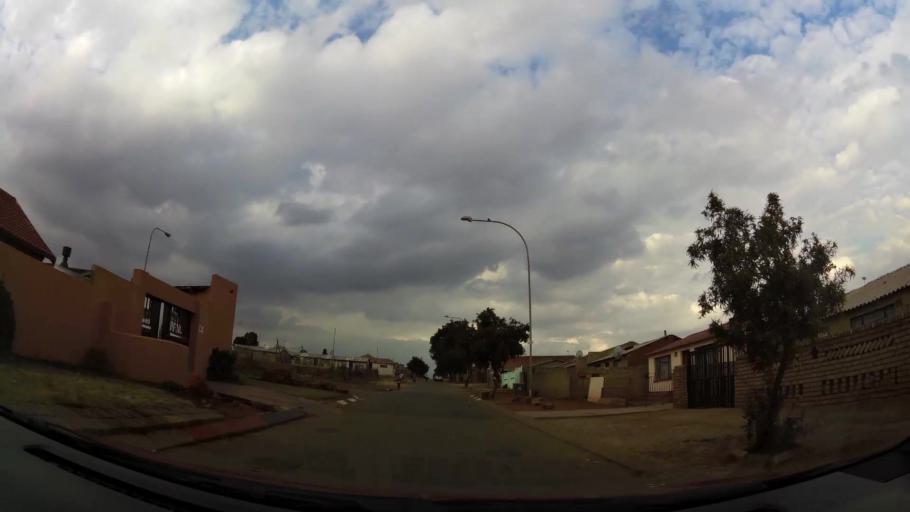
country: ZA
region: Gauteng
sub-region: City of Johannesburg Metropolitan Municipality
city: Soweto
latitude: -26.2451
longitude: 27.8135
